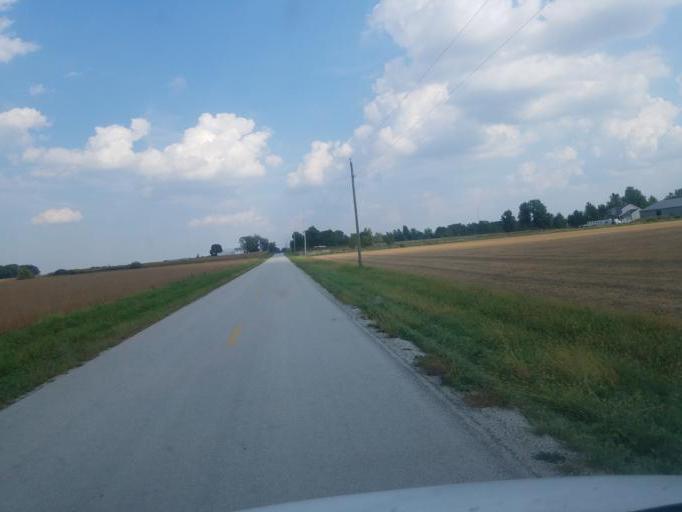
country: US
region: Ohio
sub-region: Hancock County
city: Arlington
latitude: 40.8124
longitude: -83.6690
